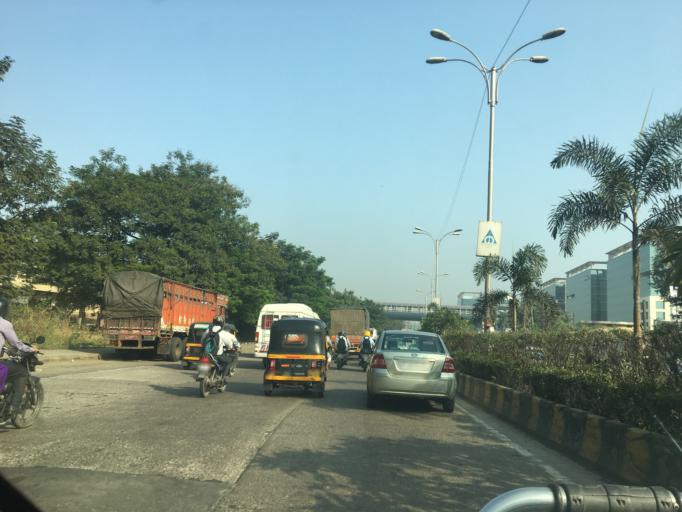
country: IN
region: Maharashtra
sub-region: Thane
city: Airoli
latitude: 19.1575
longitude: 73.0001
